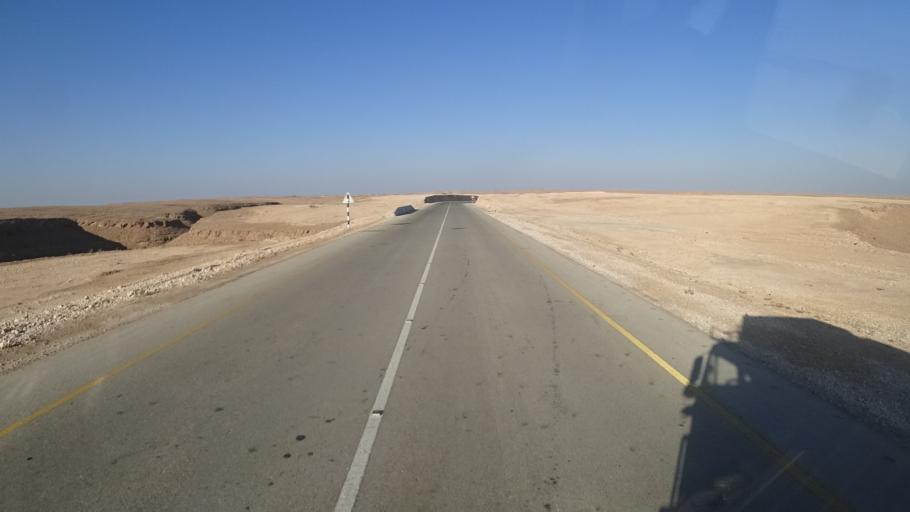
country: YE
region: Al Mahrah
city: Hawf
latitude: 17.0860
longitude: 53.0337
